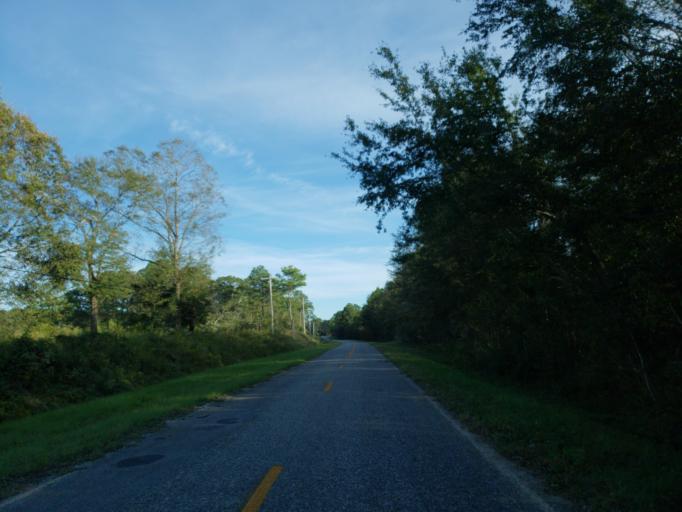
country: US
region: Georgia
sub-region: Crisp County
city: Cordele
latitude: 32.0200
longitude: -83.7367
